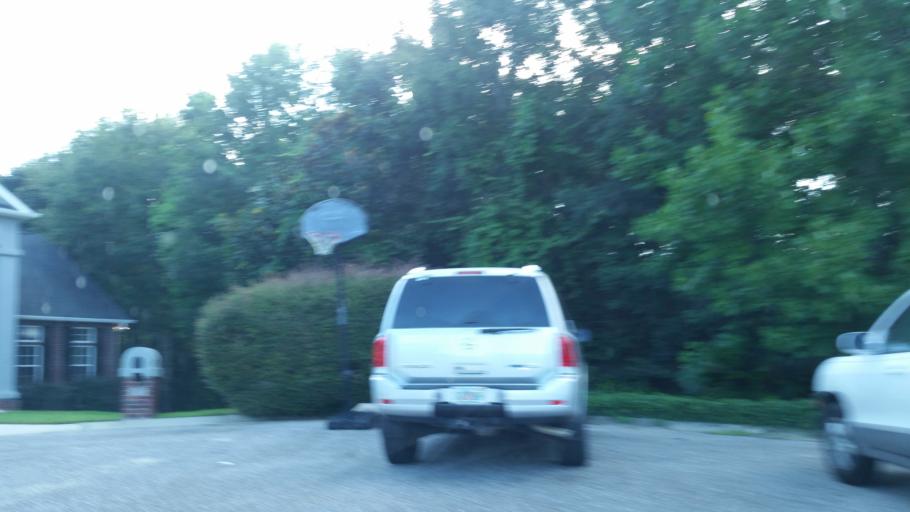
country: US
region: Florida
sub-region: Escambia County
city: Ferry Pass
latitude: 30.5105
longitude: -87.1659
